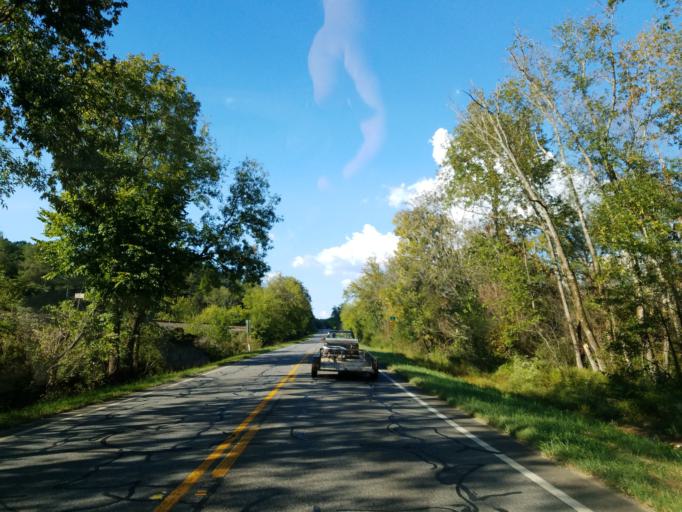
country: US
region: Georgia
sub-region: Murray County
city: Chatsworth
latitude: 34.5604
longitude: -84.7079
